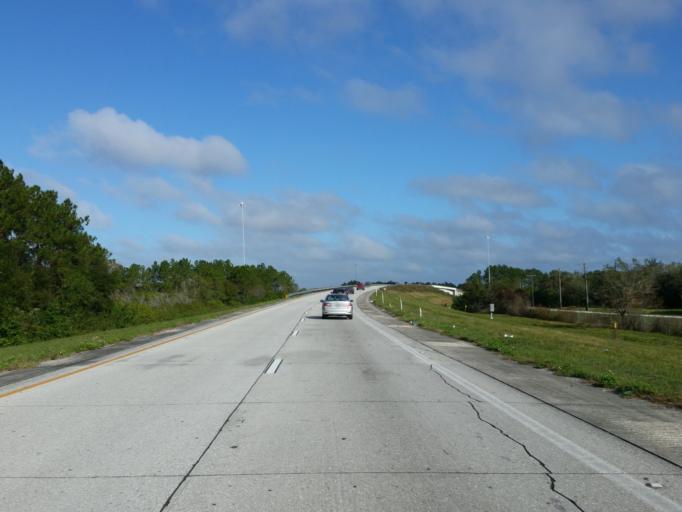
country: US
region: Florida
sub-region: Hillsborough County
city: Progress Village
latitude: 27.9051
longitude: -82.3402
